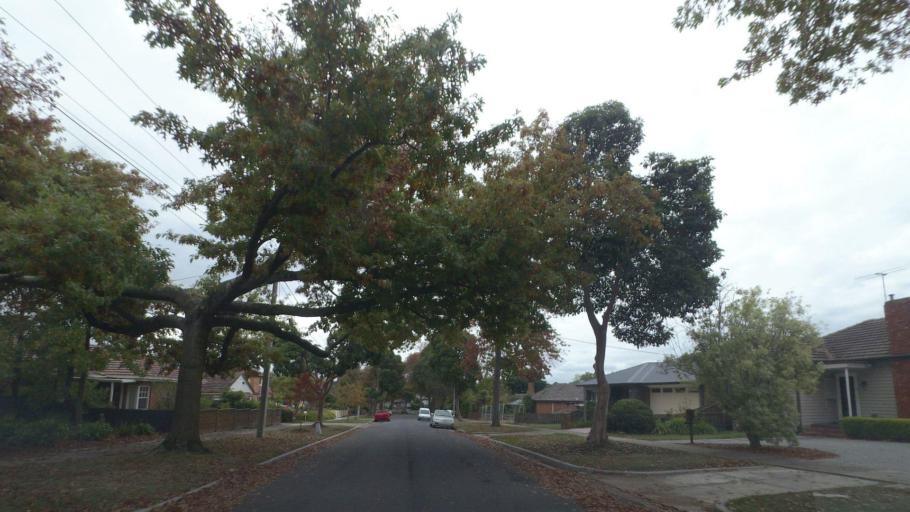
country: AU
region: Victoria
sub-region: Whitehorse
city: Nunawading
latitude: -37.8144
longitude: 145.1791
